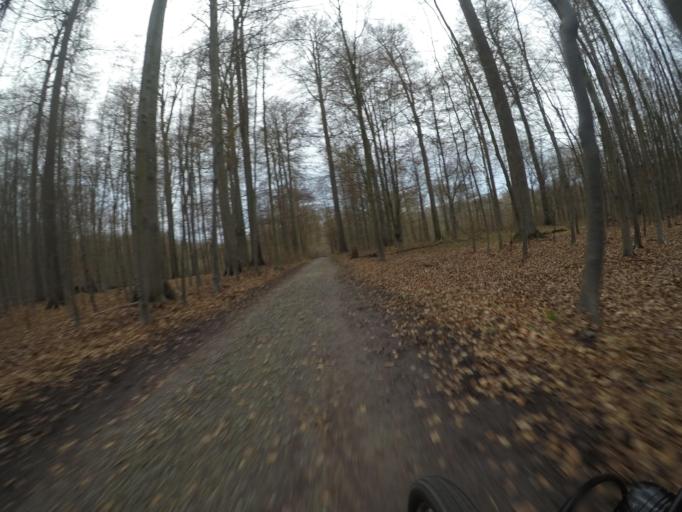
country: BE
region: Flanders
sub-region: Provincie Vlaams-Brabant
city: Hoeilaart
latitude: 50.7551
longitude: 4.4457
